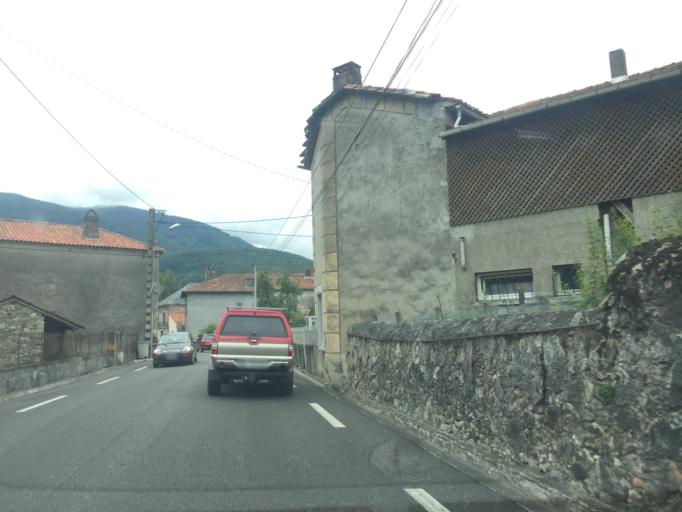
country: FR
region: Midi-Pyrenees
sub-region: Departement de la Haute-Garonne
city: Gourdan-Polignan
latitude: 42.9774
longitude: 0.6264
